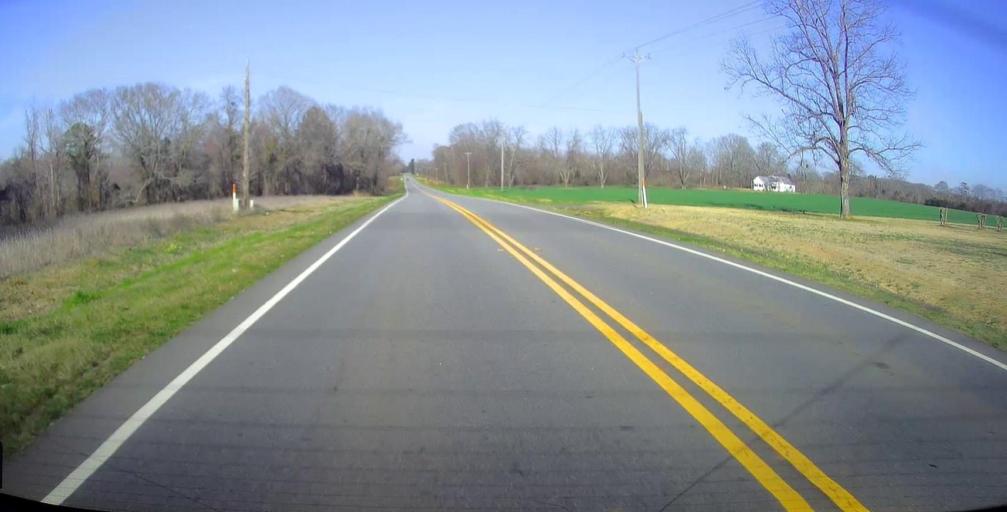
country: US
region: Georgia
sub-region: Macon County
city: Montezuma
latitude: 32.2974
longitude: -83.9126
